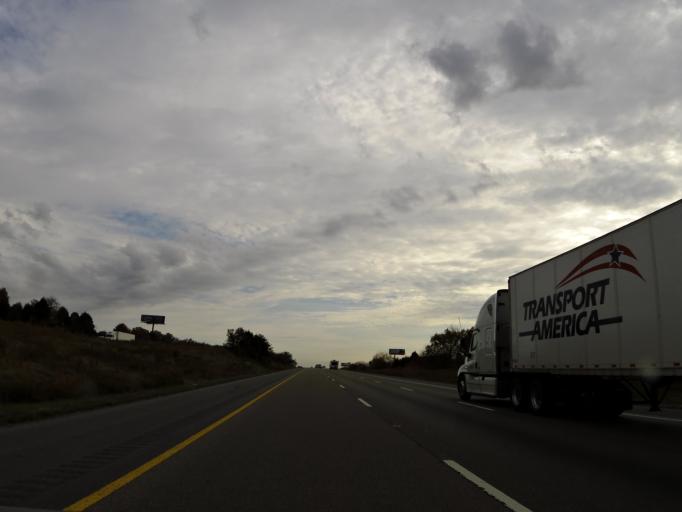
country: US
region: Tennessee
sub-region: Jefferson County
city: New Market
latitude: 35.9872
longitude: -83.5816
